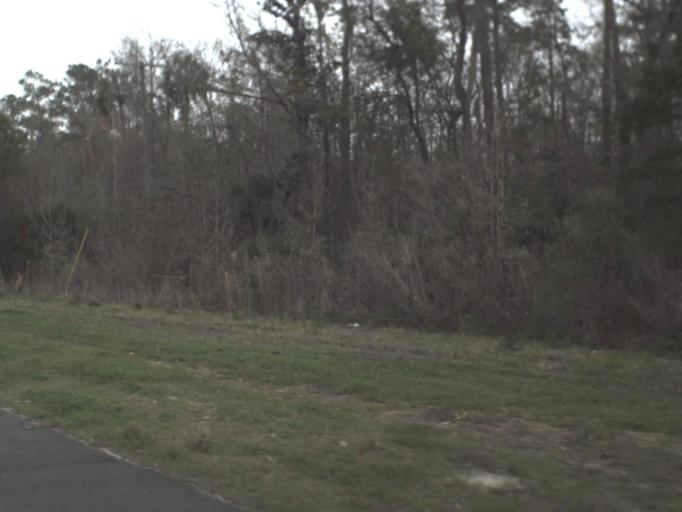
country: US
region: Florida
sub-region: Wakulla County
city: Crawfordville
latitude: 30.1797
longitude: -84.2429
